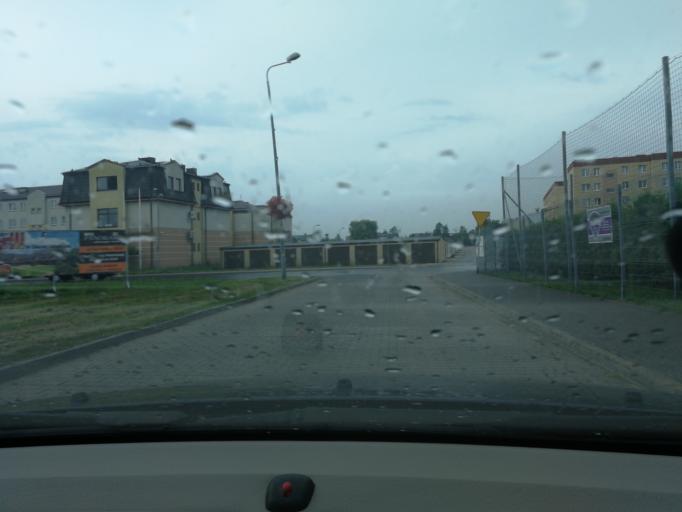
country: PL
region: Masovian Voivodeship
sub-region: Powiat zyrardowski
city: Mszczonow
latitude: 51.9776
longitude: 20.5269
